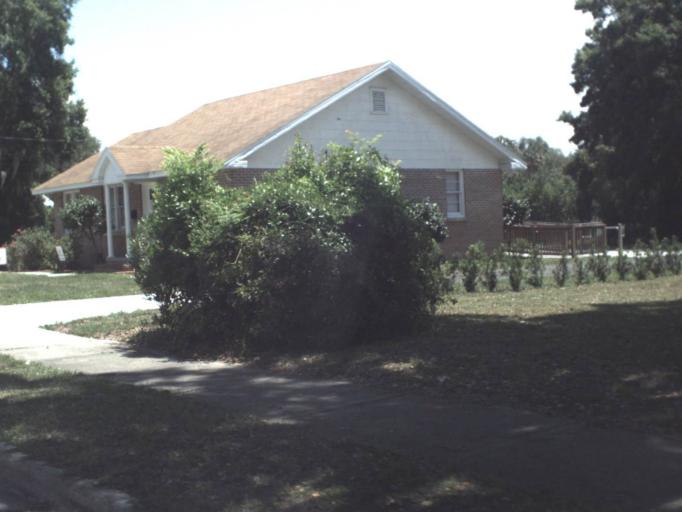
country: US
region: Florida
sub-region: Putnam County
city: Crescent City
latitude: 29.4354
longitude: -81.5104
